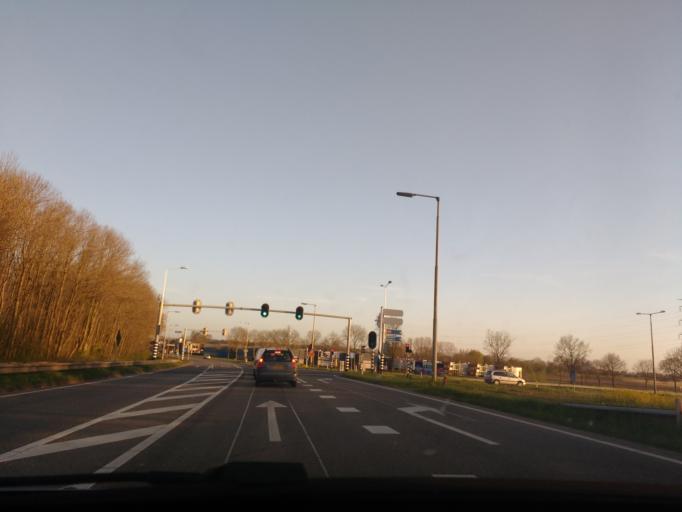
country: NL
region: Gelderland
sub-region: Gemeente Overbetuwe
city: Oosterhout
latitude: 51.8931
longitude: 5.8368
